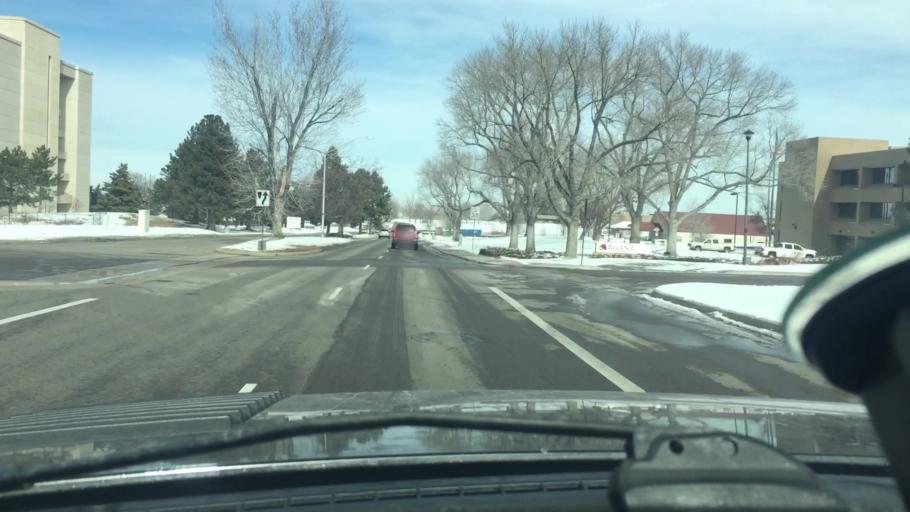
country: US
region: Colorado
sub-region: Adams County
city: Northglenn
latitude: 39.9151
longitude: -104.9851
